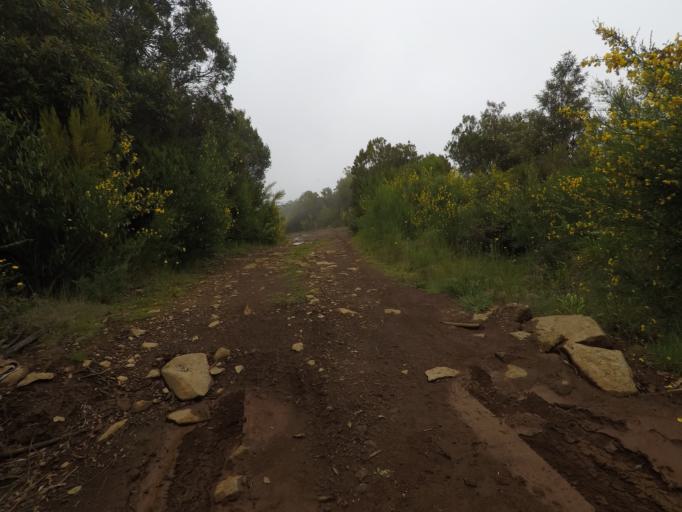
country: PT
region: Madeira
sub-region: Sao Vicente
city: Sao Vicente
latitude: 32.7700
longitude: -17.0558
